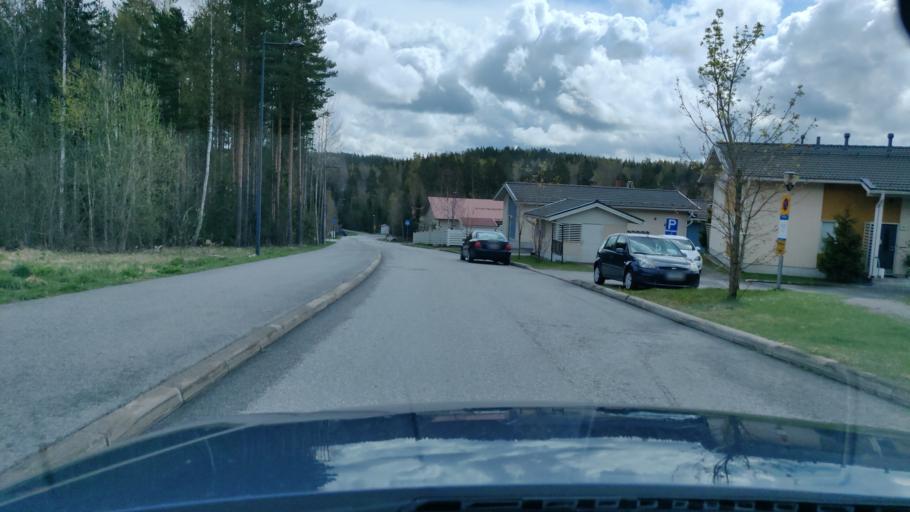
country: FI
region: Uusimaa
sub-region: Helsinki
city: Nurmijaervi
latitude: 60.3630
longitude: 24.7265
